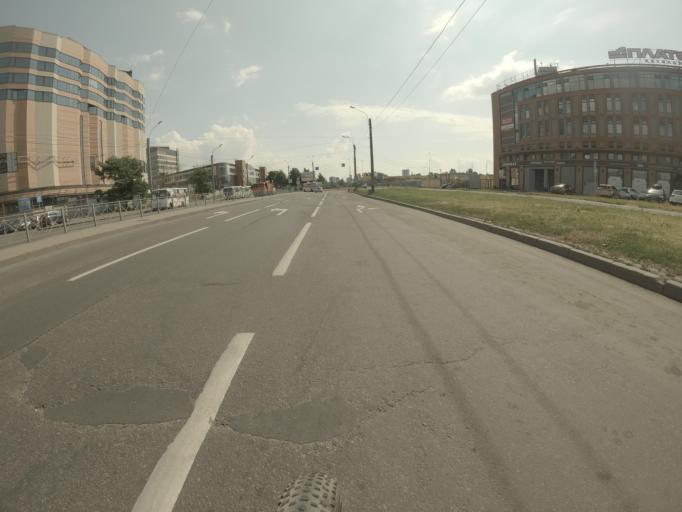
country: RU
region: St.-Petersburg
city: Krasnogvargeisky
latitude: 59.9329
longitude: 30.4353
